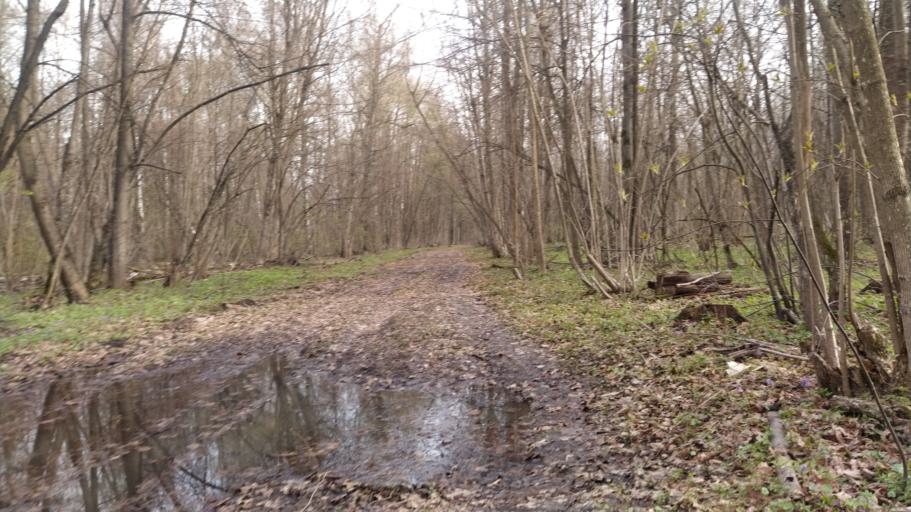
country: RU
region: Chuvashia
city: Novyye Lapsary
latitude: 56.1360
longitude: 47.1203
